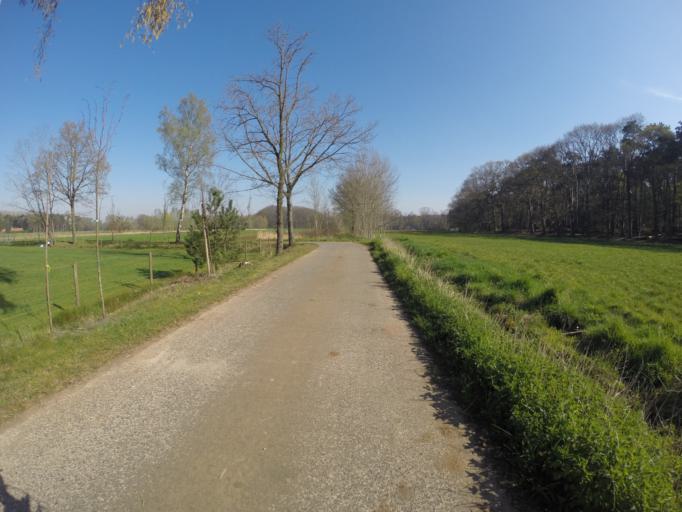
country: BE
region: Flanders
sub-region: Provincie West-Vlaanderen
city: Beernem
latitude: 51.1033
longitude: 3.3667
